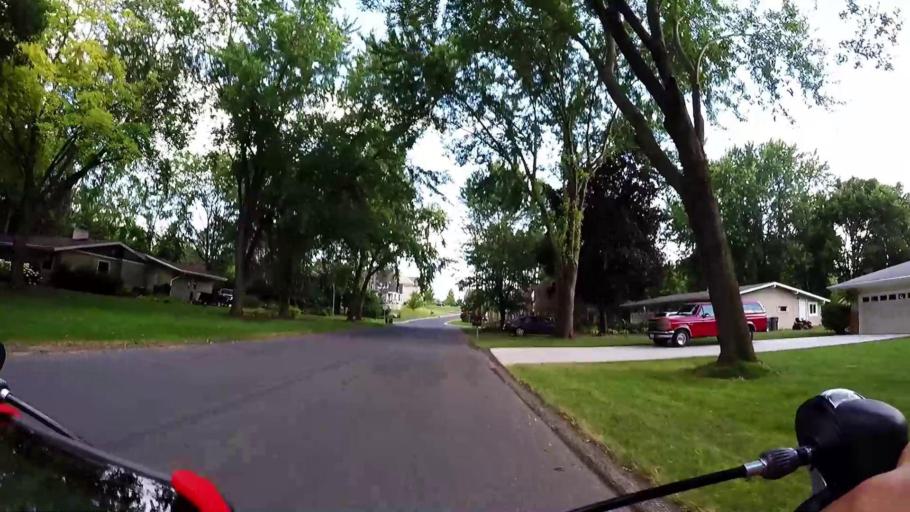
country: US
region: Minnesota
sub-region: Hennepin County
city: Minnetonka
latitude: 44.8804
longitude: -93.4997
